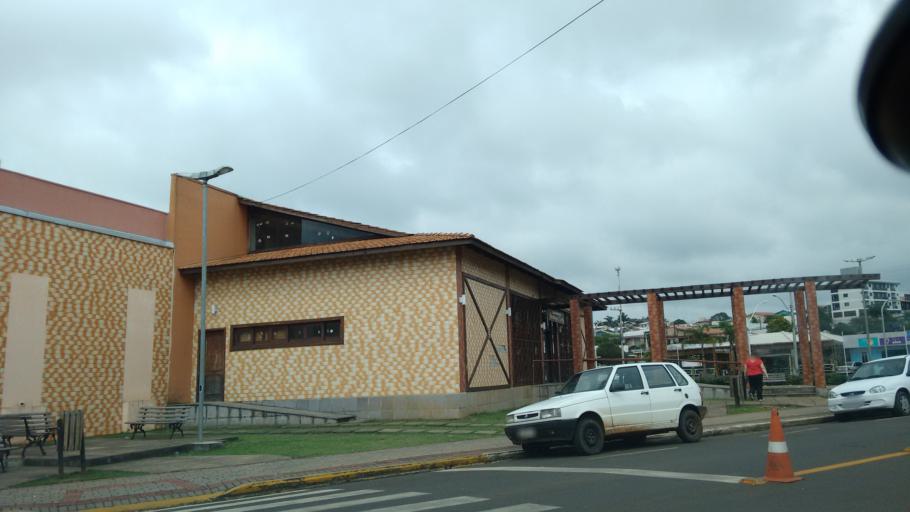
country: BR
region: Santa Catarina
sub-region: Videira
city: Videira
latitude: -27.0222
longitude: -50.9266
